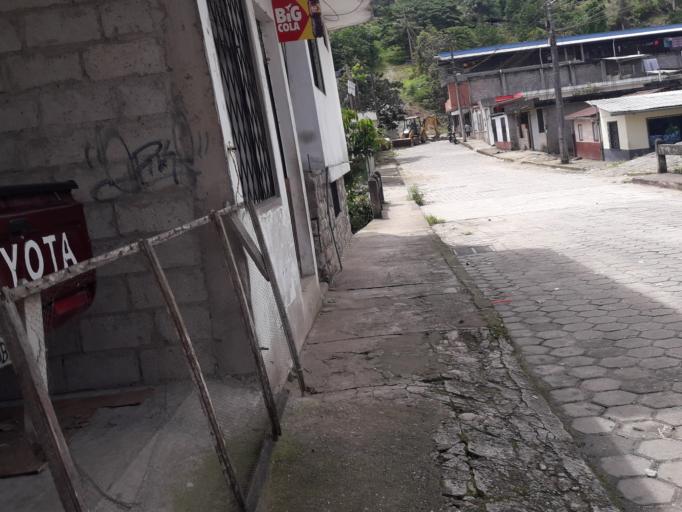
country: EC
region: Napo
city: Tena
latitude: -1.0044
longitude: -77.8087
